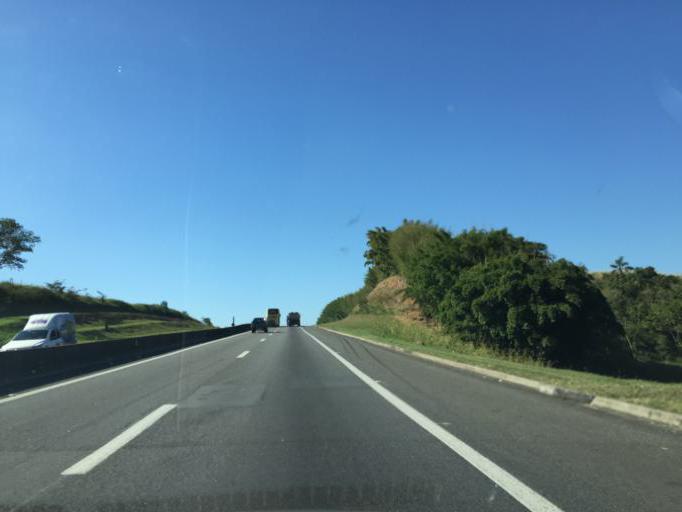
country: BR
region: Sao Paulo
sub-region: Lorena
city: Lorena
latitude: -22.6967
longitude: -45.0293
